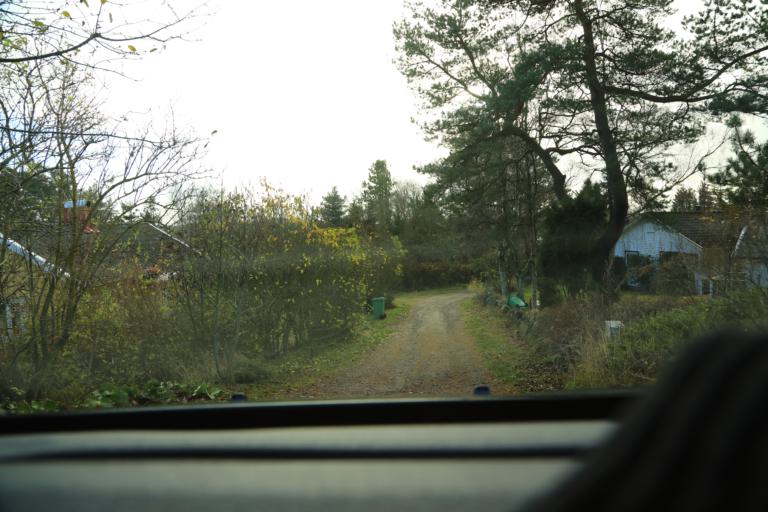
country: SE
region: Halland
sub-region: Varbergs Kommun
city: Varberg
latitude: 57.1698
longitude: 12.2179
